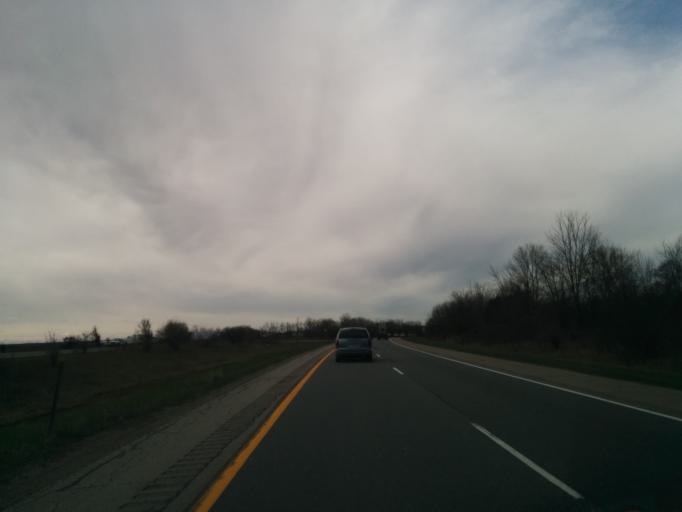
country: US
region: Michigan
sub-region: Ottawa County
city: Zeeland
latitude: 42.8038
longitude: -85.9869
